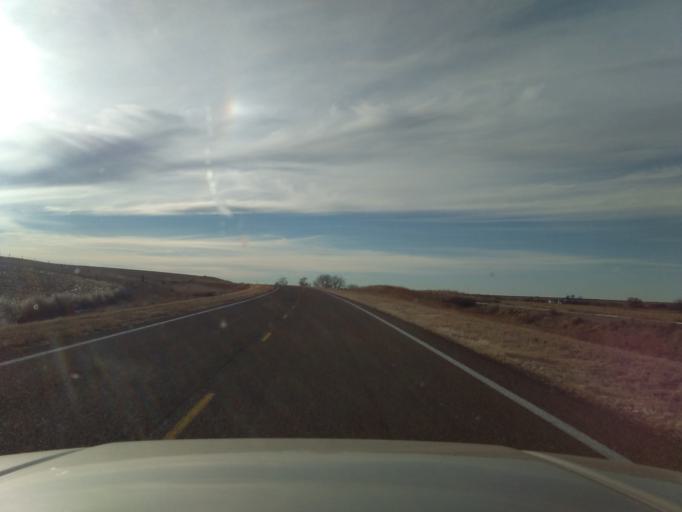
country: US
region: Kansas
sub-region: Norton County
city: Norton
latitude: 39.7515
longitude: -100.1415
